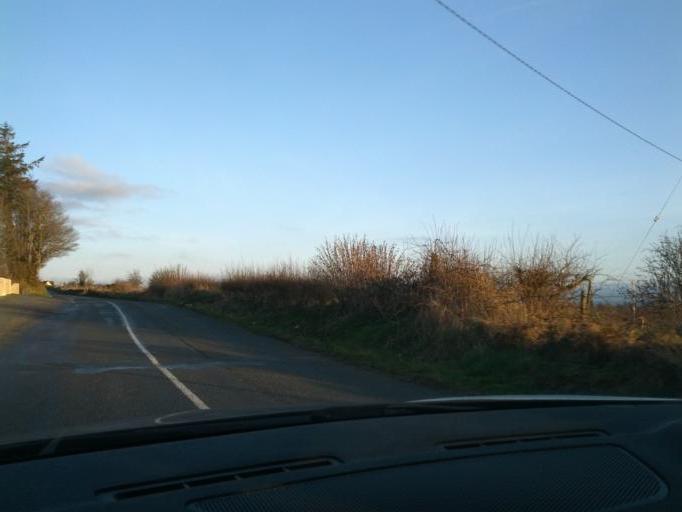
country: IE
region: Connaught
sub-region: Sligo
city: Tobercurry
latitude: 54.0502
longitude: -8.6984
